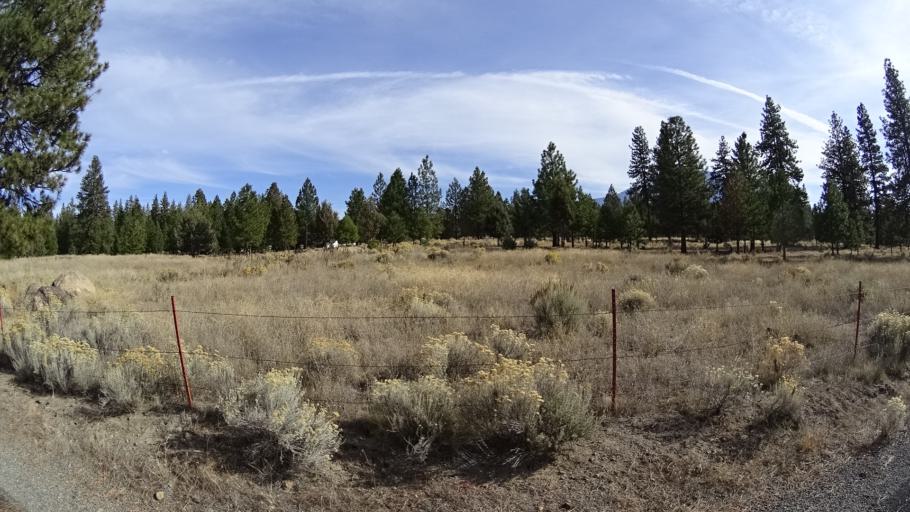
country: US
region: California
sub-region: Siskiyou County
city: Weed
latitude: 41.4962
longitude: -122.3808
